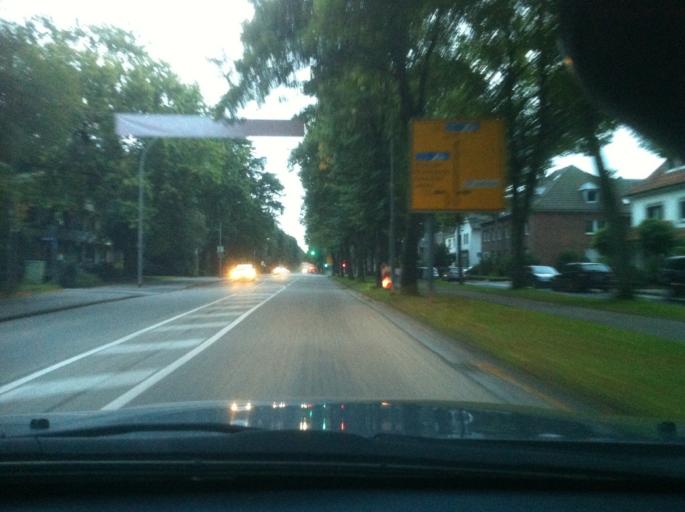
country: DE
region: North Rhine-Westphalia
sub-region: Regierungsbezirk Dusseldorf
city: Kleve
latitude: 51.7757
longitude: 6.1388
